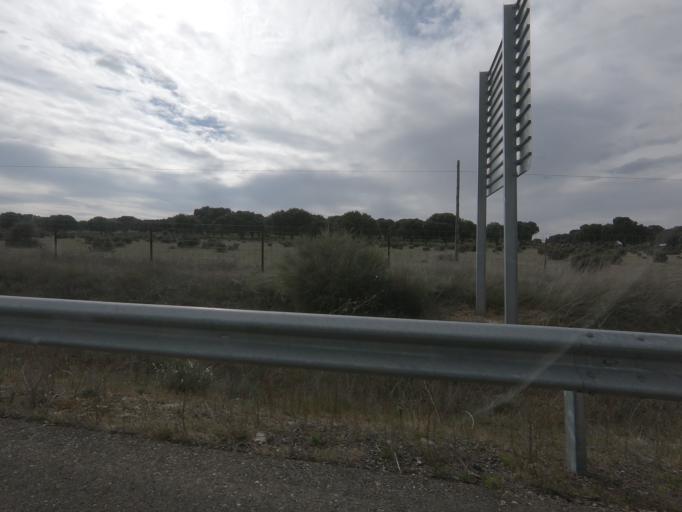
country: ES
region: Castille and Leon
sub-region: Provincia de Salamanca
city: Robleda
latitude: 40.4531
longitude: -6.5912
